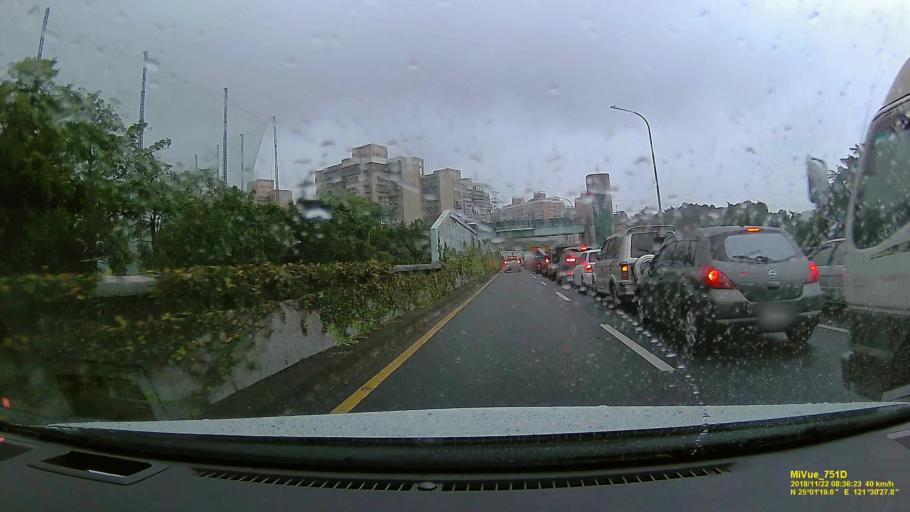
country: TW
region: Taipei
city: Taipei
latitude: 25.0222
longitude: 121.5078
